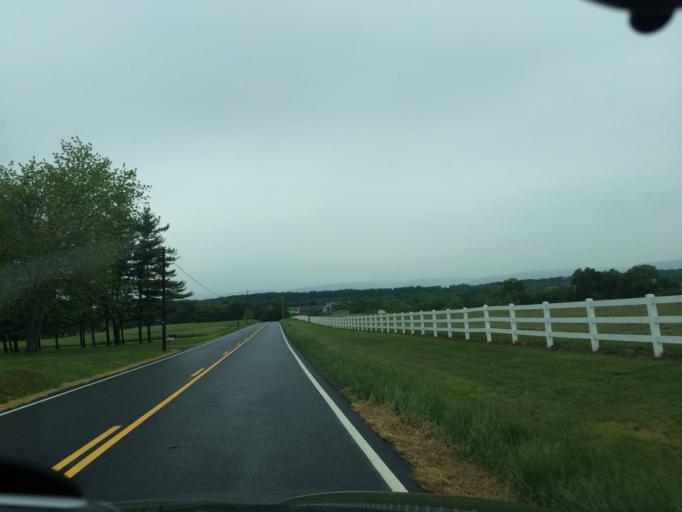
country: US
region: Maryland
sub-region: Frederick County
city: Woodsboro
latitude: 39.6021
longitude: -77.2853
